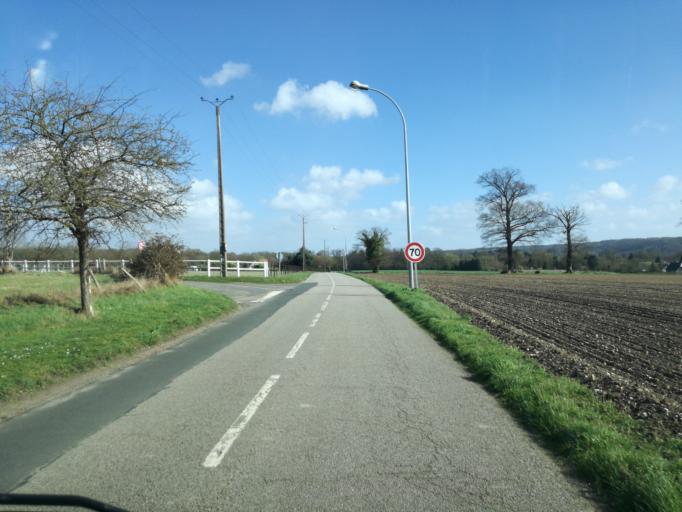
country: FR
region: Haute-Normandie
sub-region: Departement de la Seine-Maritime
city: Sahurs
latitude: 49.3578
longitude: 0.9482
